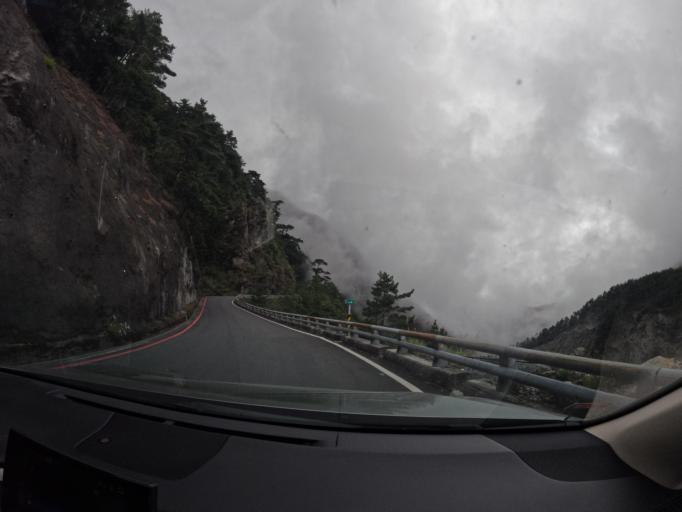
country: TW
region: Taiwan
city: Lugu
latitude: 23.2689
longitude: 120.9769
